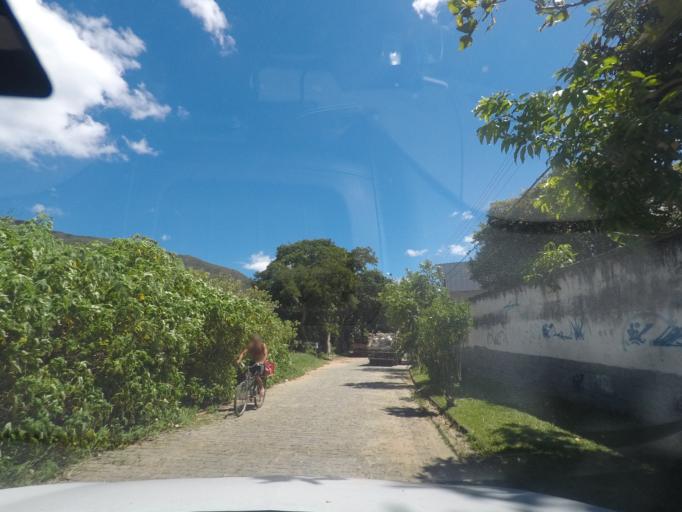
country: BR
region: Rio de Janeiro
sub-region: Teresopolis
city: Teresopolis
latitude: -22.4334
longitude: -42.9749
